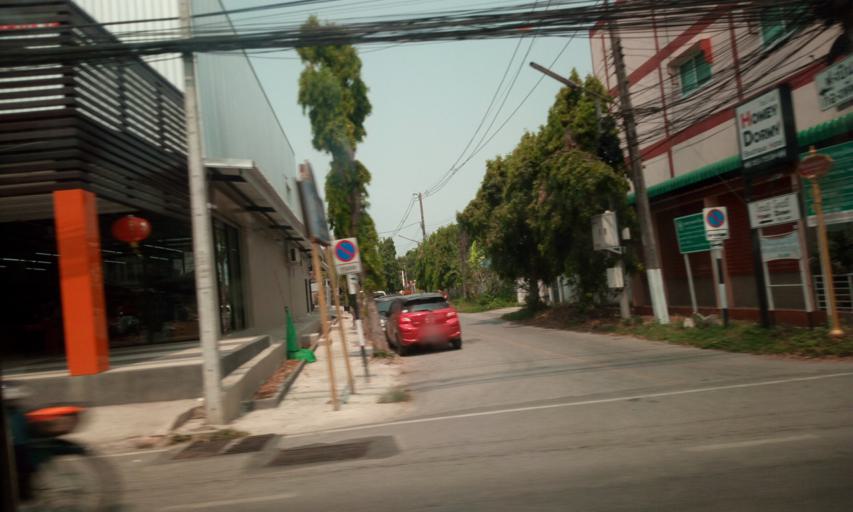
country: TH
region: Chiang Rai
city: Chiang Rai
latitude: 19.8889
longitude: 99.8303
